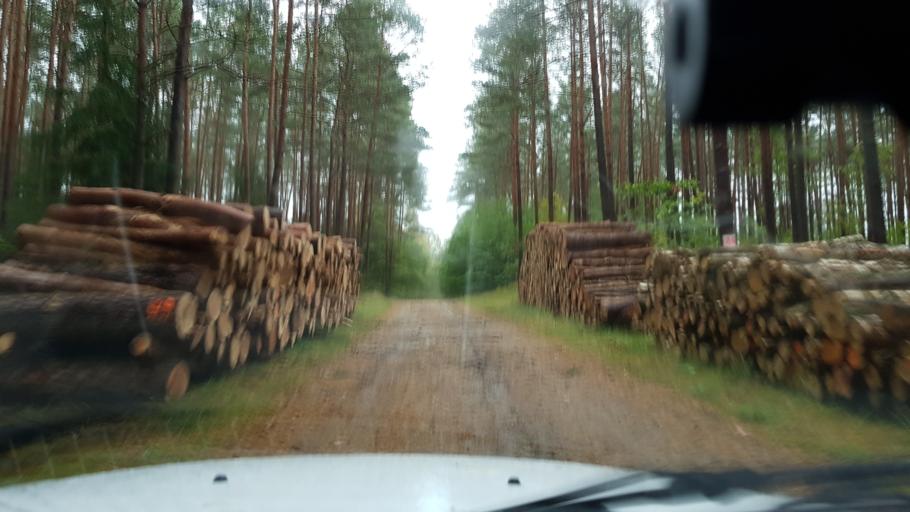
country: PL
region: West Pomeranian Voivodeship
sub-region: Powiat goleniowski
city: Przybiernow
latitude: 53.7275
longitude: 14.8106
